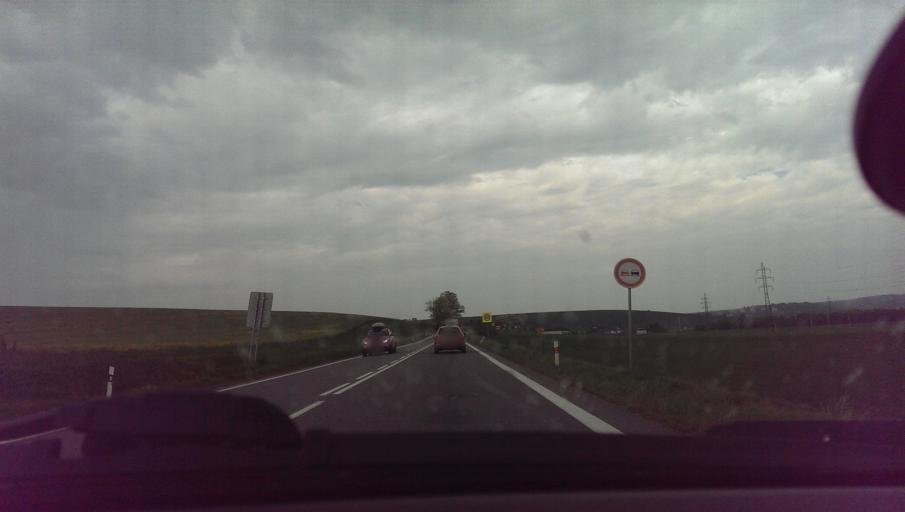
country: CZ
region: South Moravian
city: Letonice
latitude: 49.1499
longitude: 16.9663
